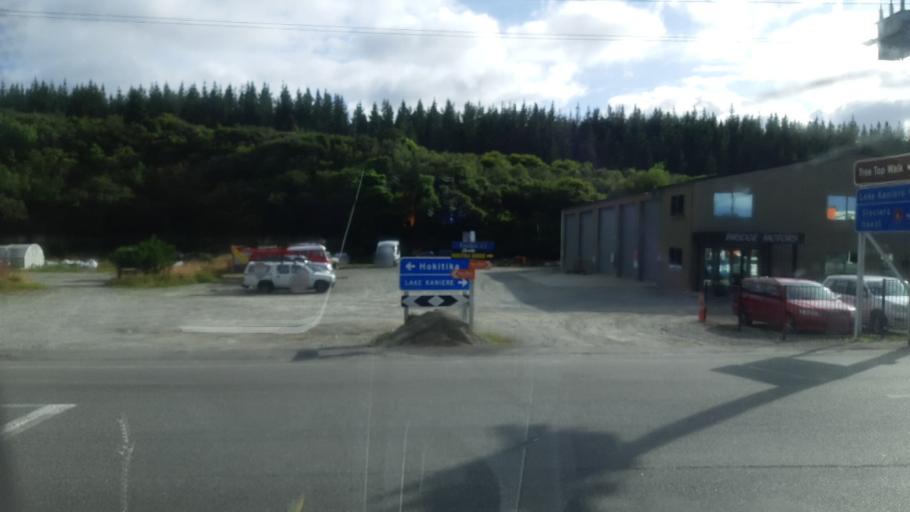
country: NZ
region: West Coast
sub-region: Westland District
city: Hokitika
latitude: -42.7451
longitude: 171.0009
